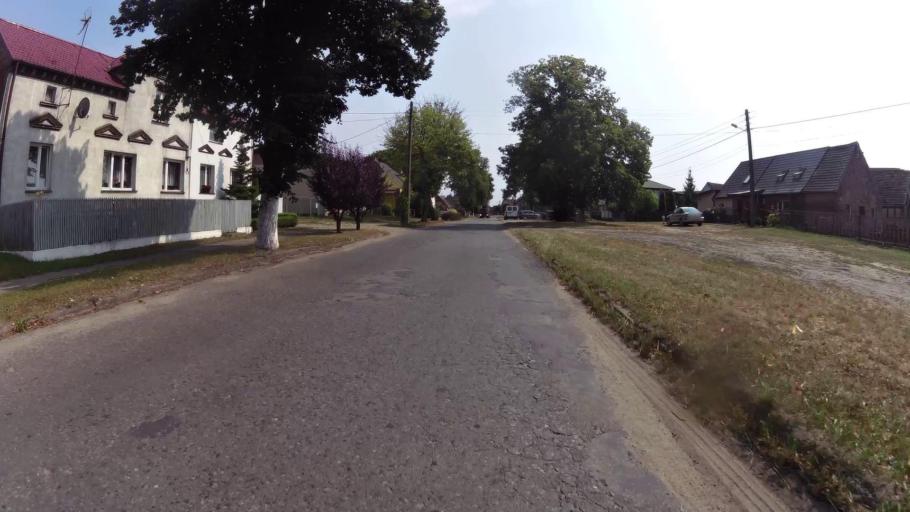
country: PL
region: West Pomeranian Voivodeship
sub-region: Powiat mysliborski
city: Mysliborz
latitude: 52.8467
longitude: 14.7865
